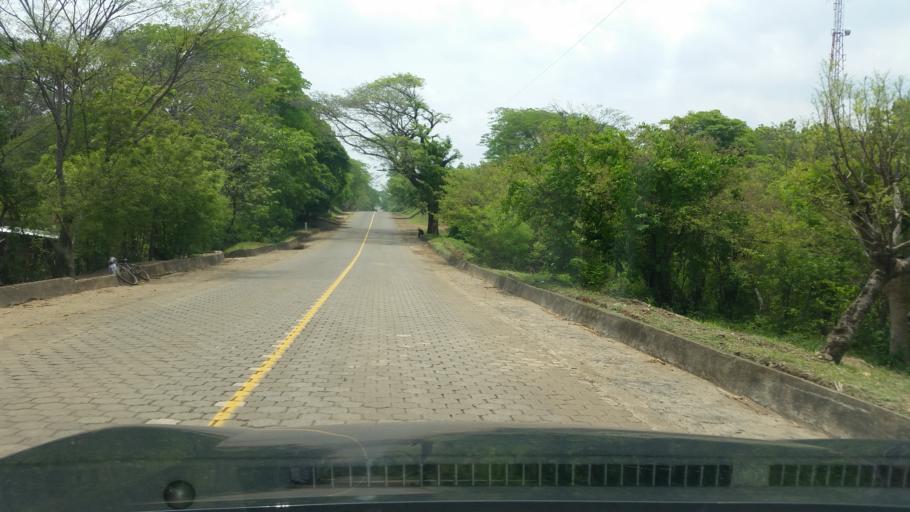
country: NI
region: Managua
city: Carlos Fonseca Amador
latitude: 11.9511
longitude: -86.5100
